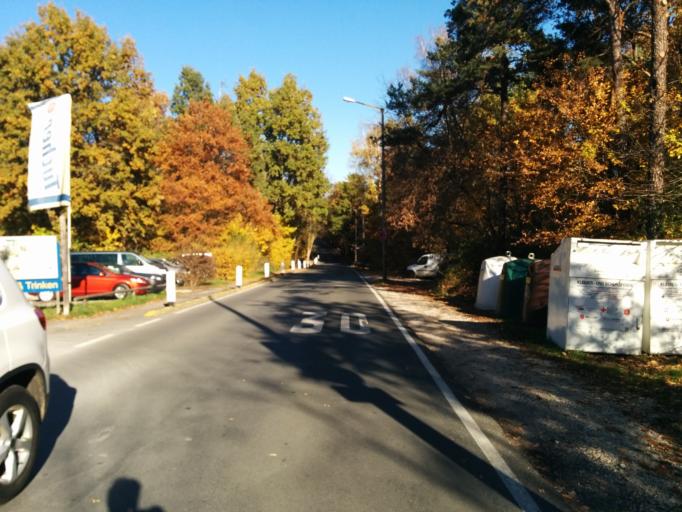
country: DE
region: Bavaria
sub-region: Regierungsbezirk Mittelfranken
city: Nuernberg
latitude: 49.4744
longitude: 11.1284
